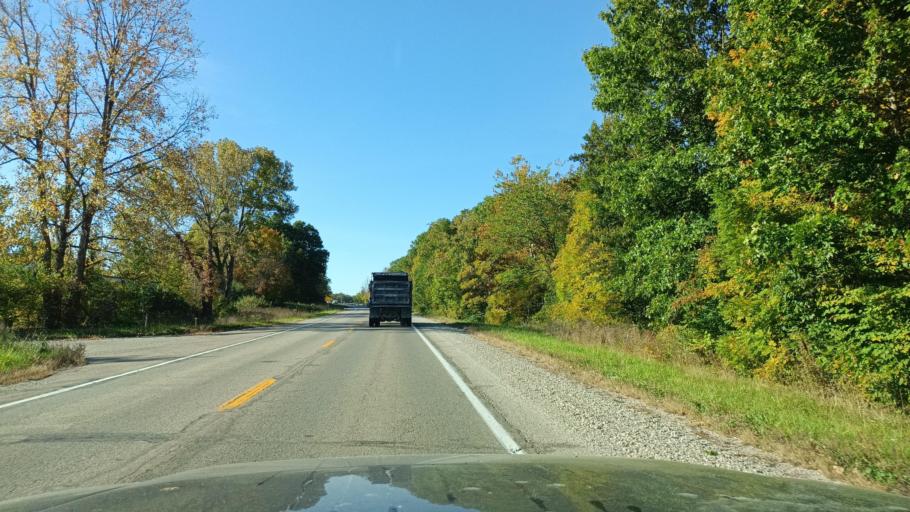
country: US
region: Illinois
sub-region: Clark County
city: Marshall
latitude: 39.4307
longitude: -87.6905
